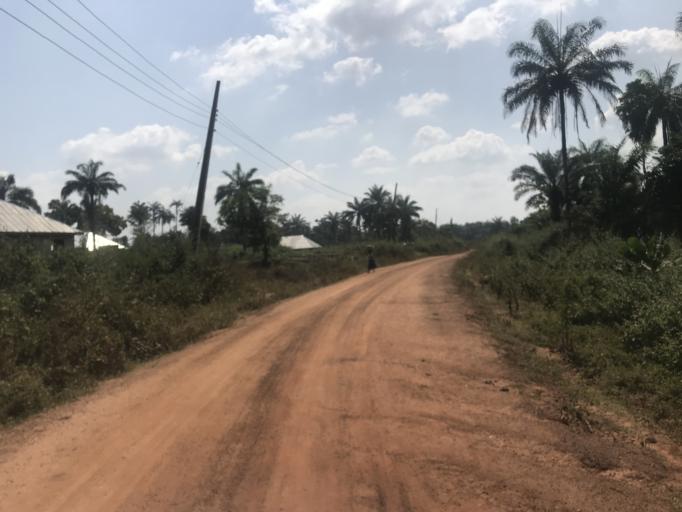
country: NG
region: Osun
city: Iragbiji
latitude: 7.8825
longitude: 4.7008
